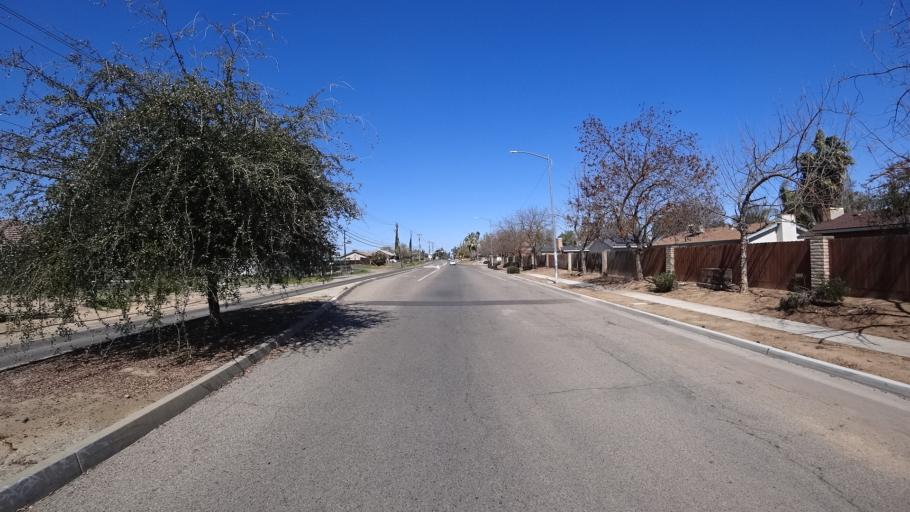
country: US
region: California
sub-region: Fresno County
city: West Park
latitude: 36.7761
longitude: -119.8713
